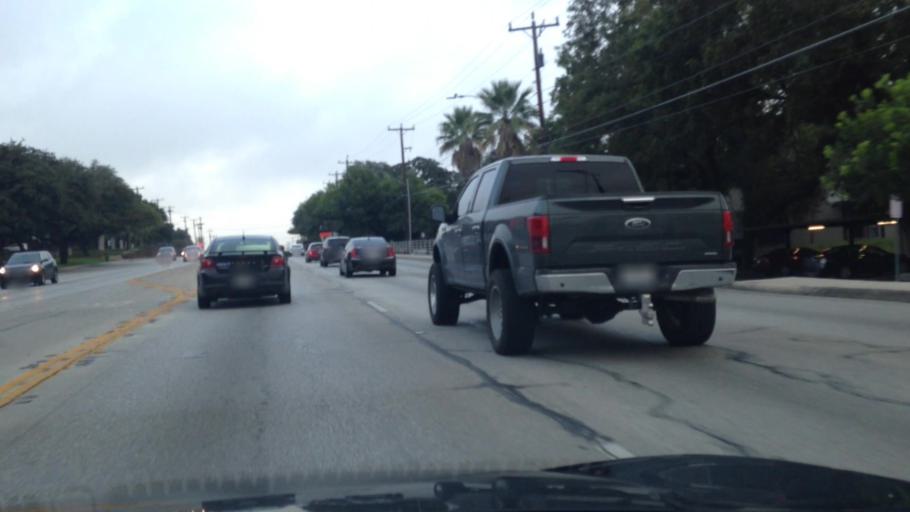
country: US
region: Texas
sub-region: Bexar County
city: Balcones Heights
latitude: 29.5079
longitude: -98.5645
